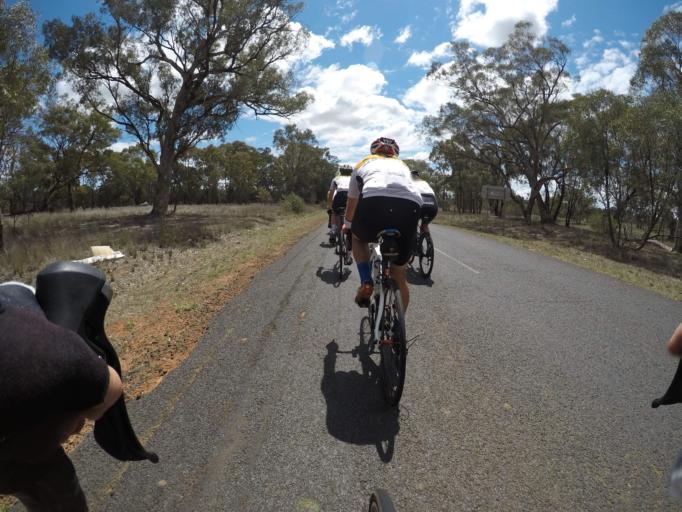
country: AU
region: New South Wales
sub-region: Dubbo Municipality
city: Dubbo
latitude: -32.3927
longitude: 148.5716
